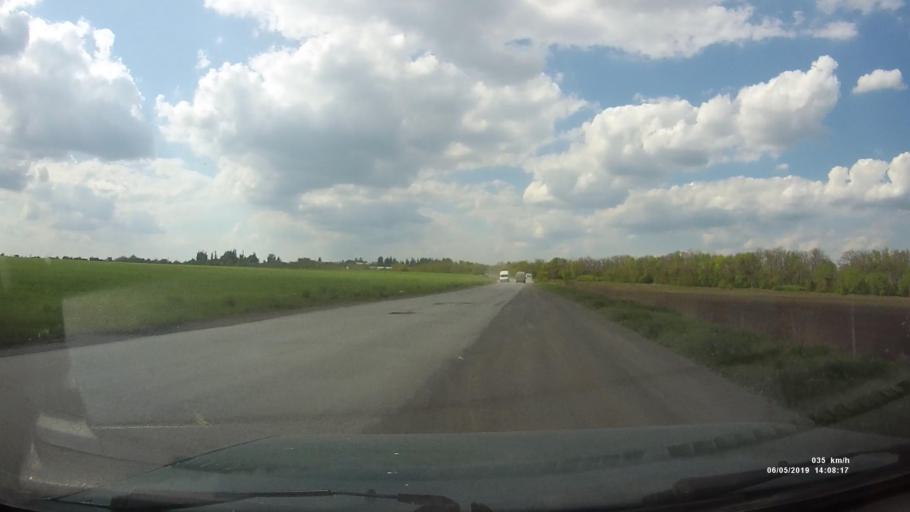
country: RU
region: Rostov
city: Shakhty
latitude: 47.6826
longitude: 40.2992
